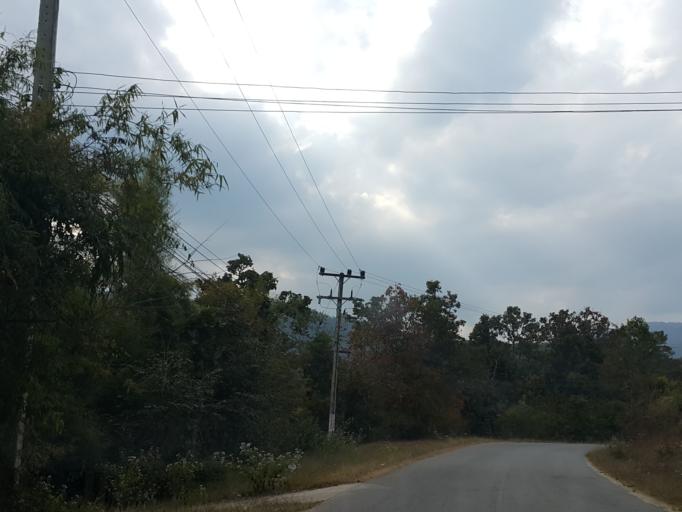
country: TH
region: Chiang Mai
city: Om Koi
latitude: 17.7974
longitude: 98.3486
